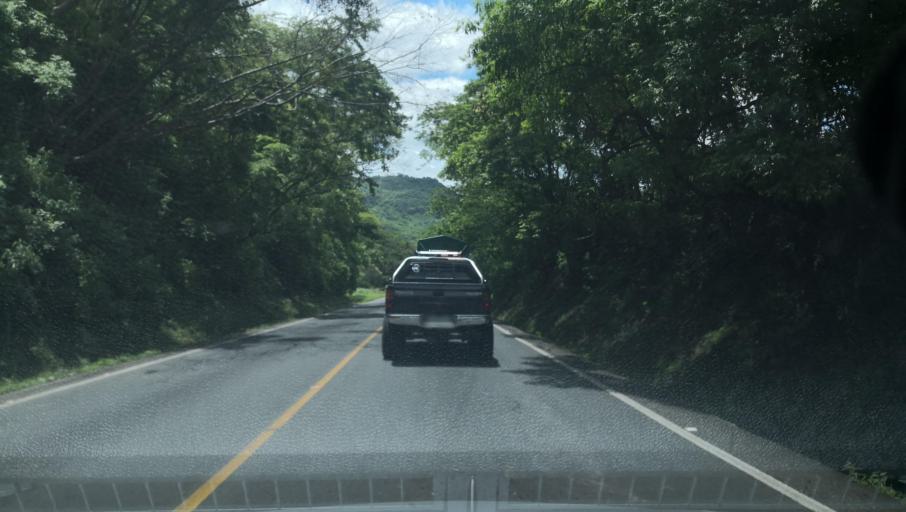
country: NI
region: Esteli
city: Condega
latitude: 13.2621
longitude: -86.3539
